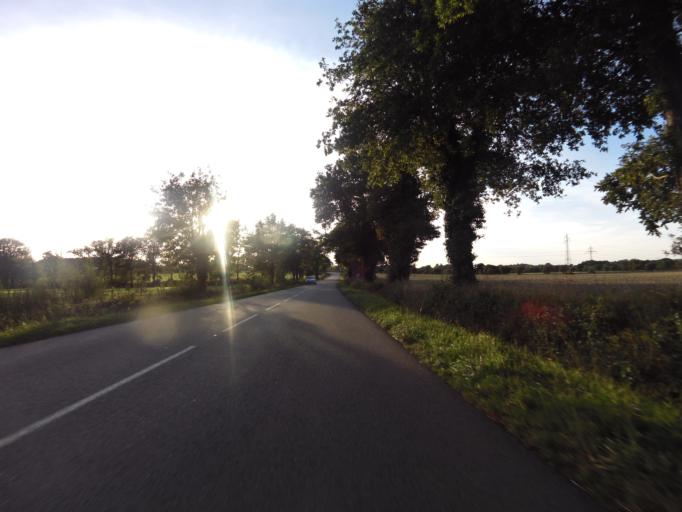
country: FR
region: Brittany
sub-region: Departement du Morbihan
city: Theix
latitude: 47.6340
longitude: -2.6257
